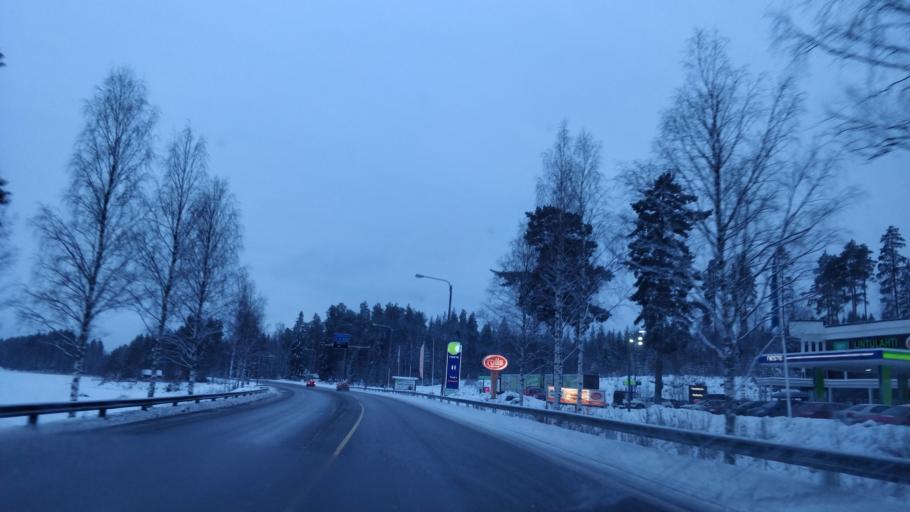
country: FI
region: Central Finland
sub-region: AEaenekoski
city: AEaenekoski
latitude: 62.8201
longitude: 25.8031
